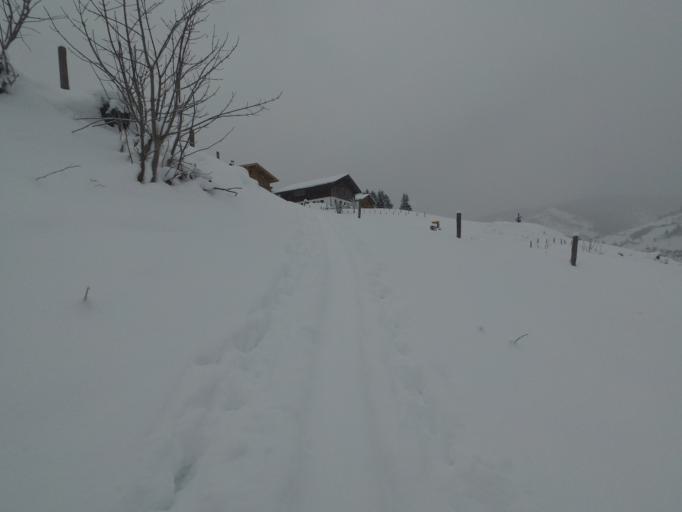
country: AT
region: Salzburg
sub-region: Politischer Bezirk Sankt Johann im Pongau
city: Wagrain
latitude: 47.3303
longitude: 13.2882
